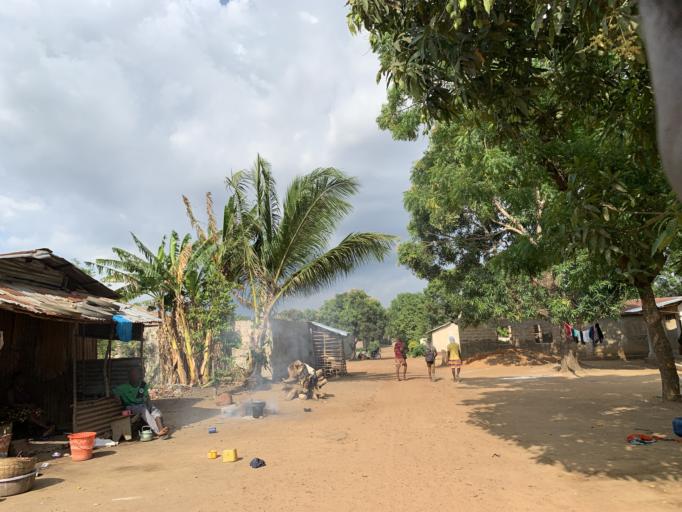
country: SL
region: Western Area
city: Waterloo
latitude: 8.3390
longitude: -13.0438
